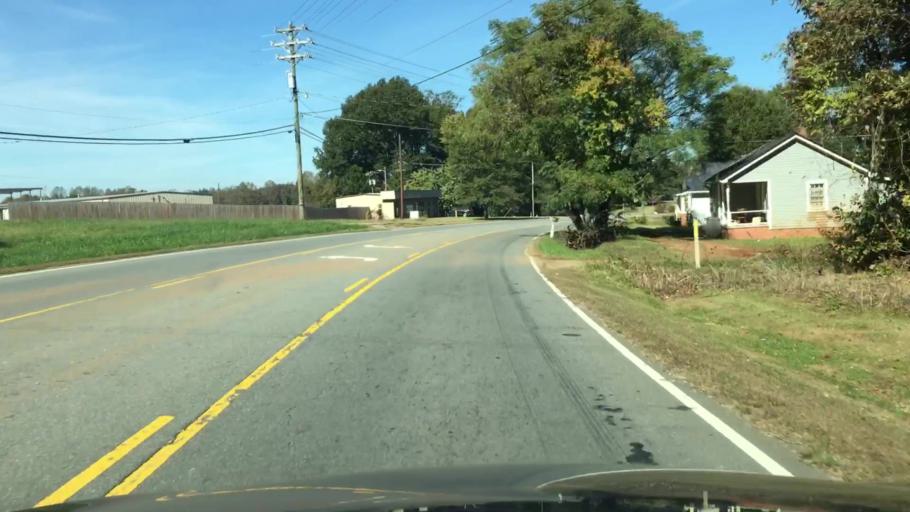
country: US
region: North Carolina
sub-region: Rockingham County
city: Reidsville
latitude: 36.3320
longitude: -79.6509
